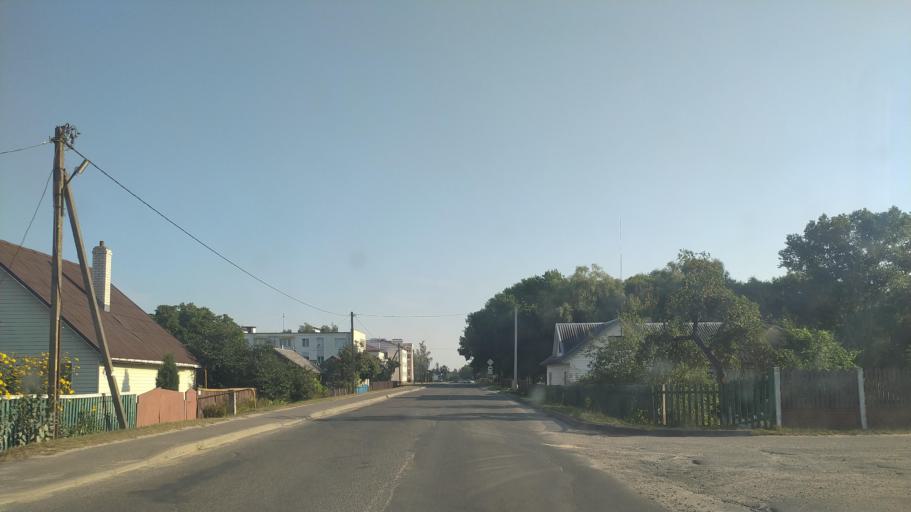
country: BY
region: Brest
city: Drahichyn
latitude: 52.1849
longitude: 25.1709
